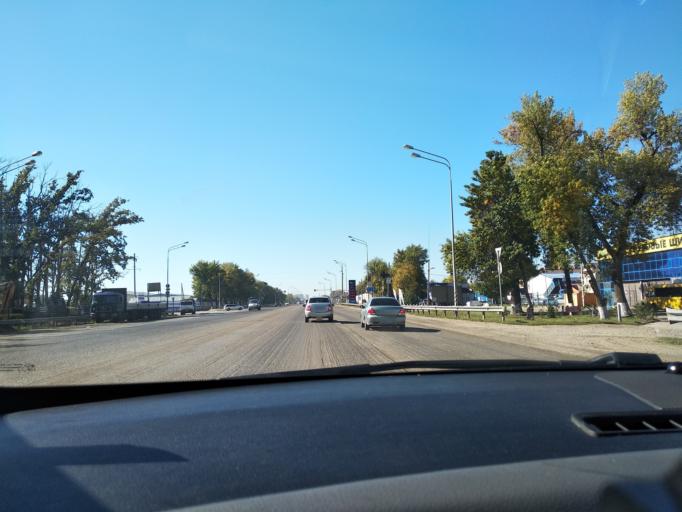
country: RU
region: Krasnodarskiy
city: Krasnodar
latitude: 45.1342
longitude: 39.0261
